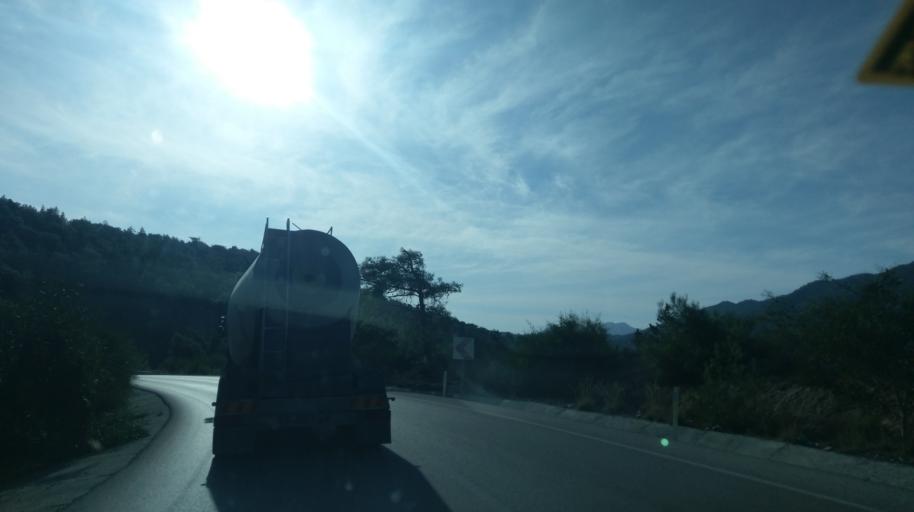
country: CY
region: Ammochostos
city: Lefkonoiko
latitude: 35.3392
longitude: 33.7160
